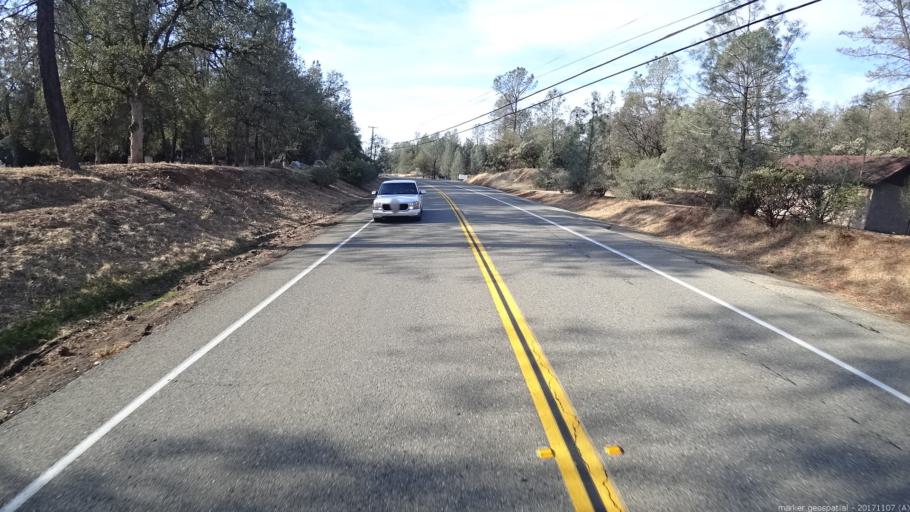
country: US
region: California
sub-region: Shasta County
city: Shasta
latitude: 40.5521
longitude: -122.4523
